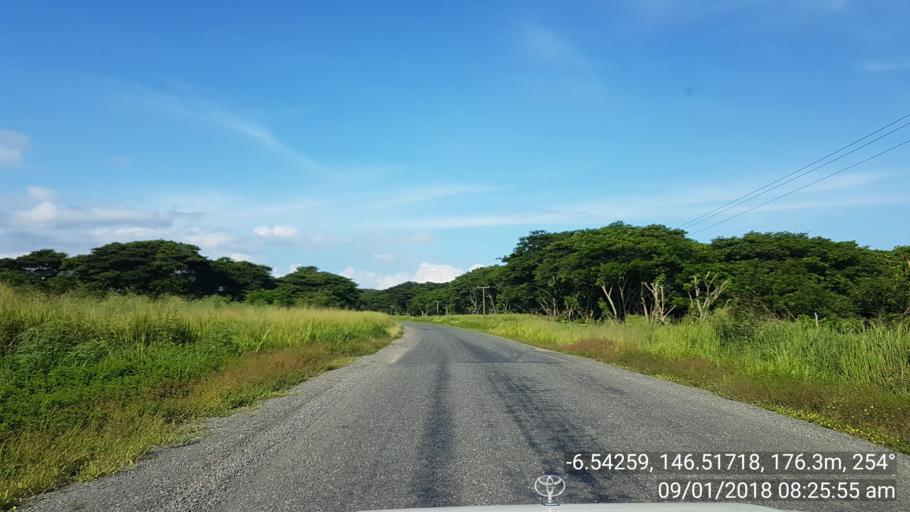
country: PG
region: Morobe
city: Lae
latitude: -6.5426
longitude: 146.5167
